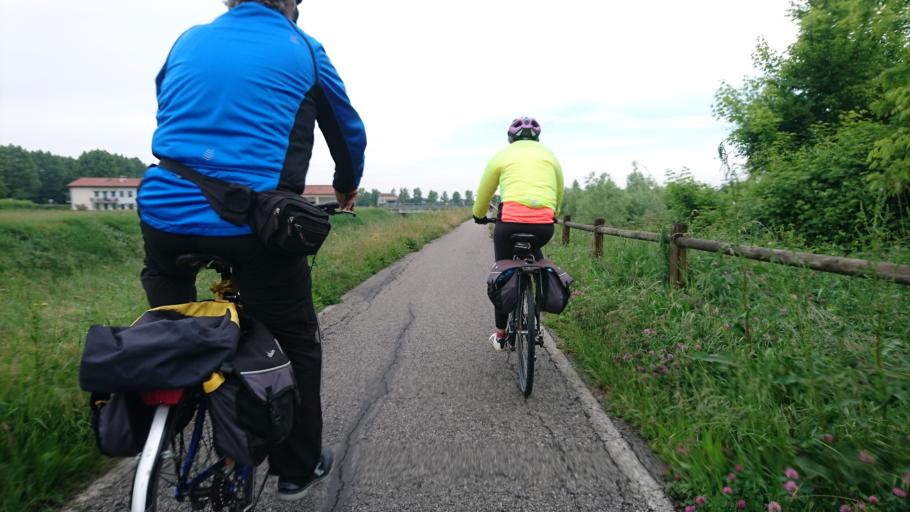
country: IT
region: Veneto
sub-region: Provincia di Padova
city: Montegrotto Terme
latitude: 45.3295
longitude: 11.7754
